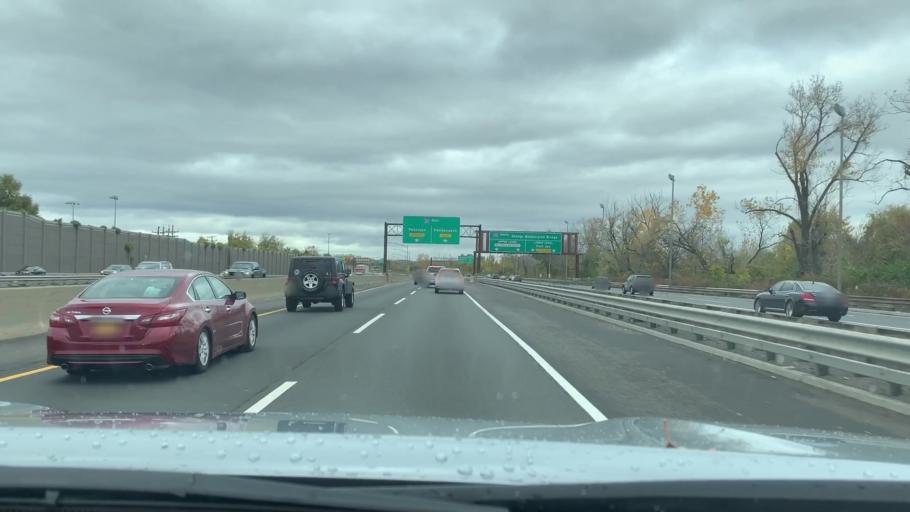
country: US
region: New Jersey
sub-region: Bergen County
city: Ridgefield Park
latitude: 40.8557
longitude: -74.0133
